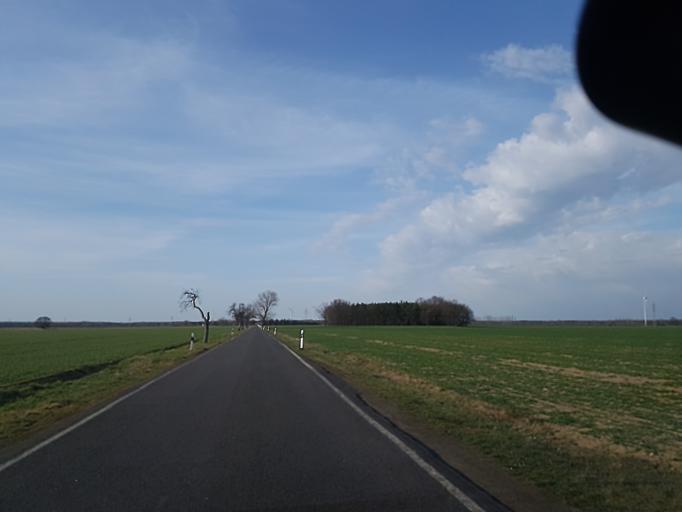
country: DE
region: Brandenburg
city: Falkenberg
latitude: 51.5335
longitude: 13.2954
